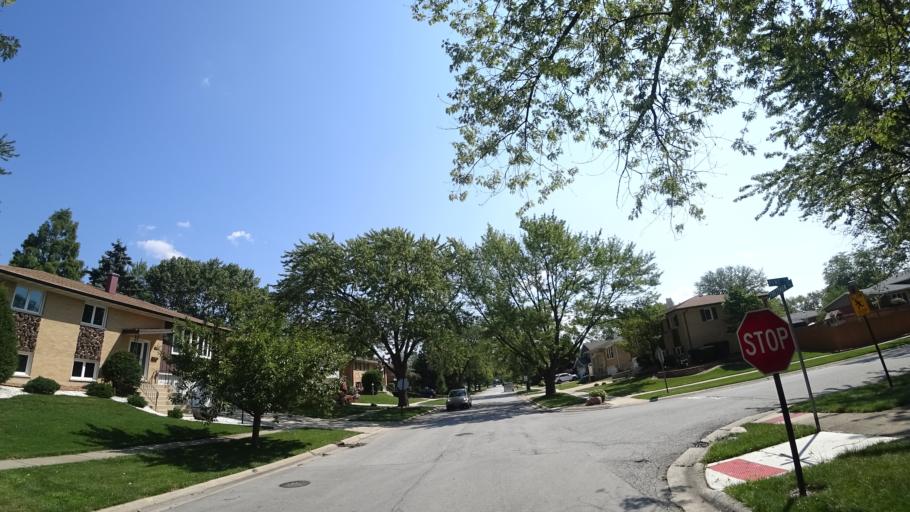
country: US
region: Illinois
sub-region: Cook County
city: Oak Forest
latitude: 41.6156
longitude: -87.7793
